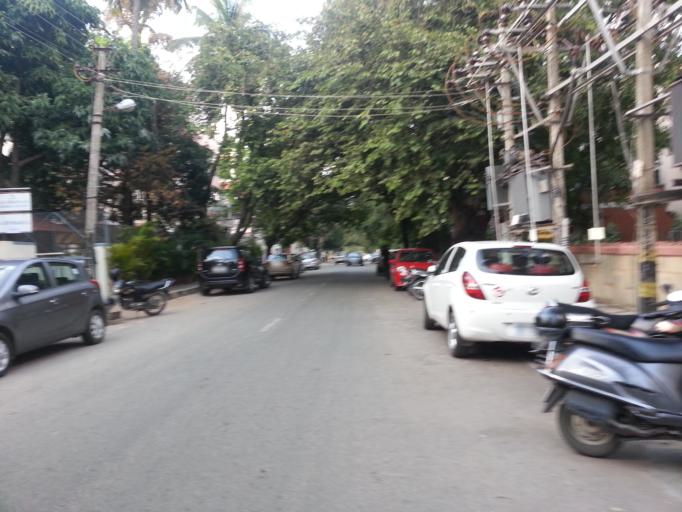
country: IN
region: Karnataka
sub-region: Bangalore Urban
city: Bangalore
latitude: 13.0044
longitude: 77.5667
